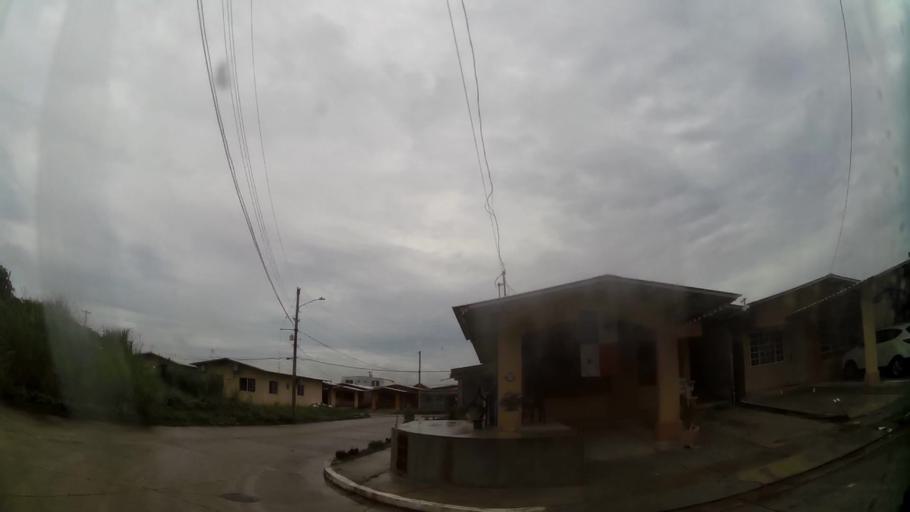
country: PA
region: Colon
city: Las Margaritas
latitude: 9.3293
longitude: -79.8841
